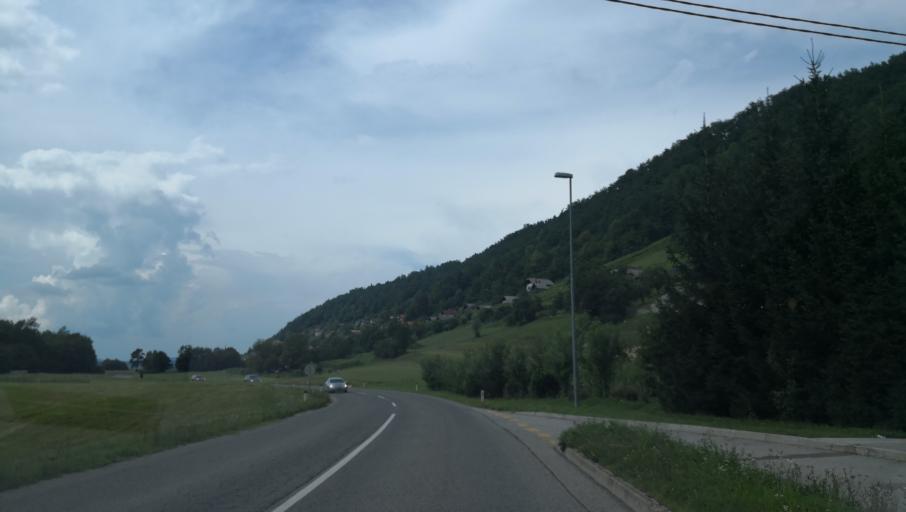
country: SI
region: Zuzemberk
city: Zuzemberk
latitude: 45.7964
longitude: 14.9830
